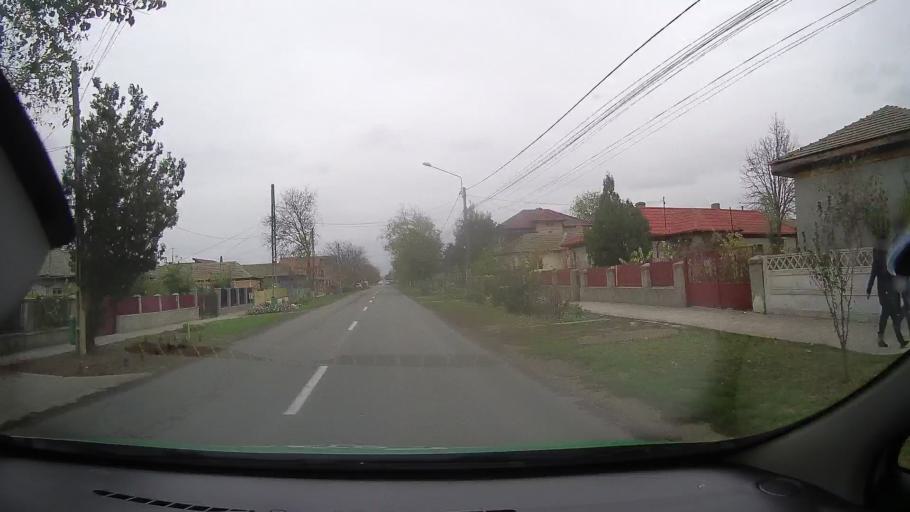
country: RO
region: Constanta
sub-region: Comuna Mihail Kogalniceanu
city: Mihail Kogalniceanu
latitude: 44.3677
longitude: 28.4626
